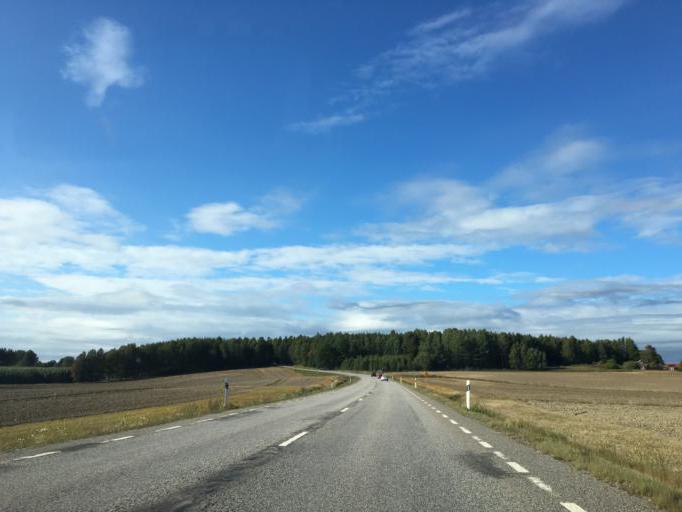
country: SE
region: Soedermanland
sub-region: Nykopings Kommun
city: Svalsta
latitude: 58.8608
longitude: 16.9144
